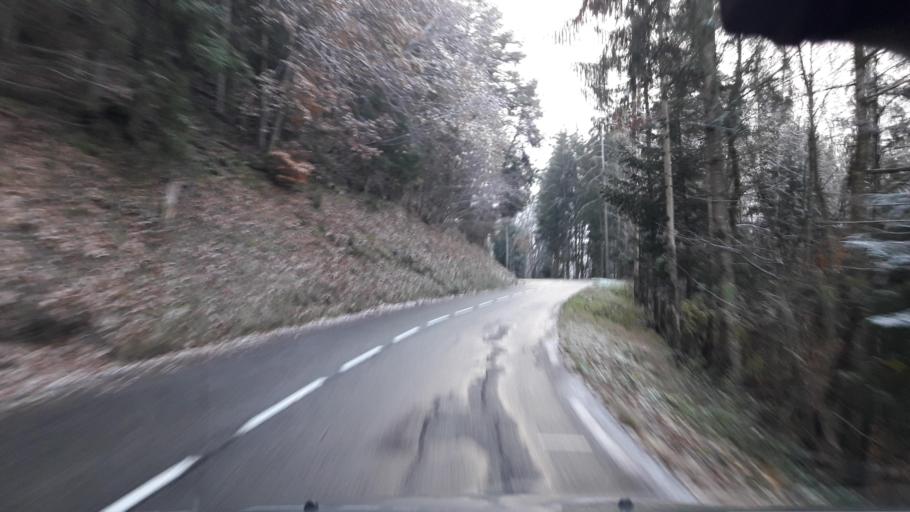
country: FR
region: Rhone-Alpes
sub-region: Departement de l'Isere
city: Allevard
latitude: 45.3906
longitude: 6.0868
